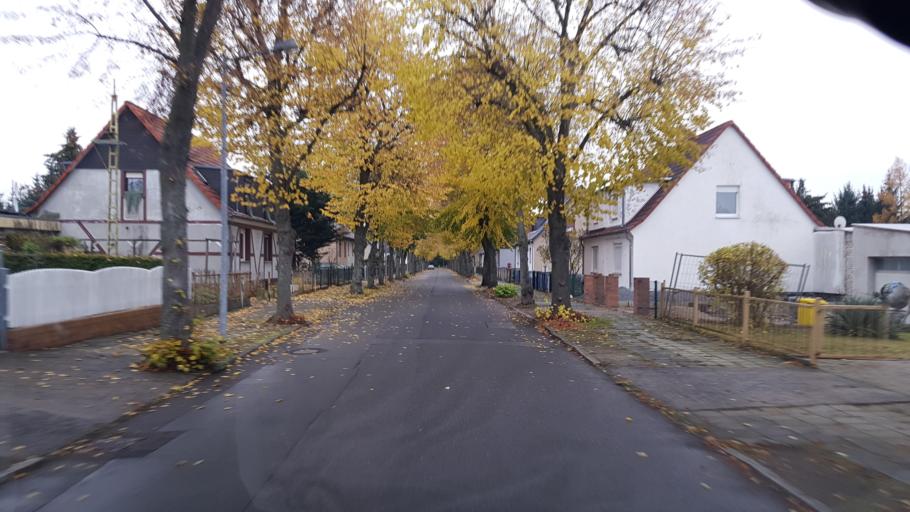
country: DE
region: Brandenburg
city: Lauchhammer
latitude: 51.4925
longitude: 13.7453
